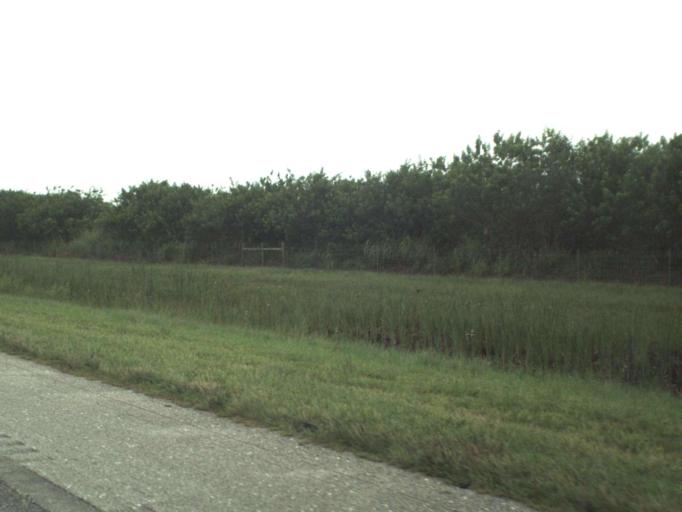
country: US
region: Florida
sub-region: Martin County
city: Hobe Sound
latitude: 27.0253
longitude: -80.2288
